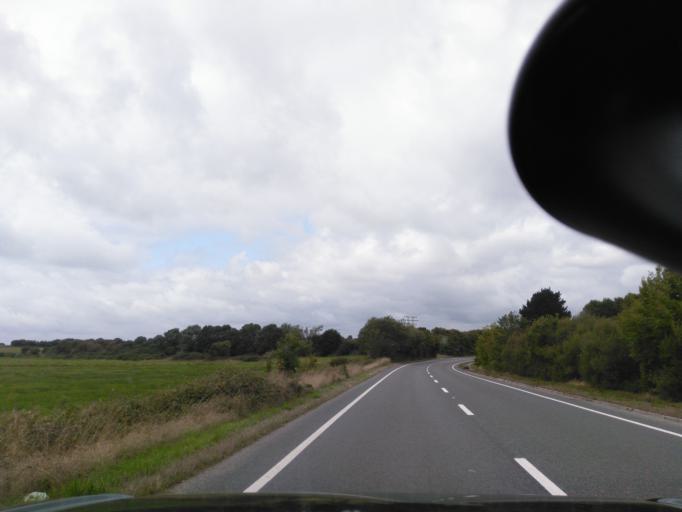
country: GB
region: England
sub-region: Dorset
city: Wareham
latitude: 50.6782
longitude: -2.1204
